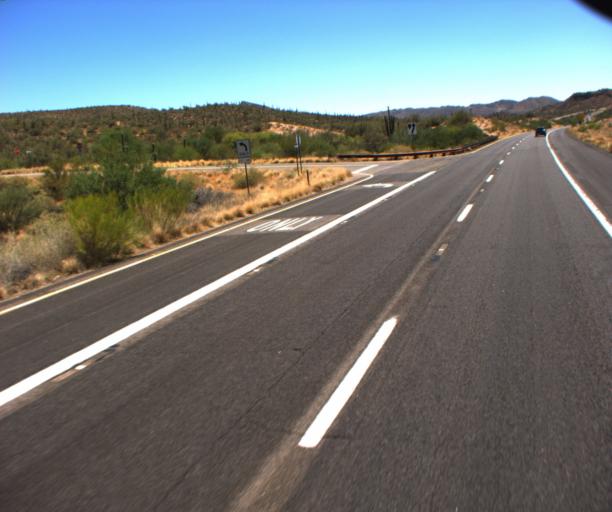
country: US
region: Arizona
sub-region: Maricopa County
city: Rio Verde
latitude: 33.7655
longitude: -111.4947
